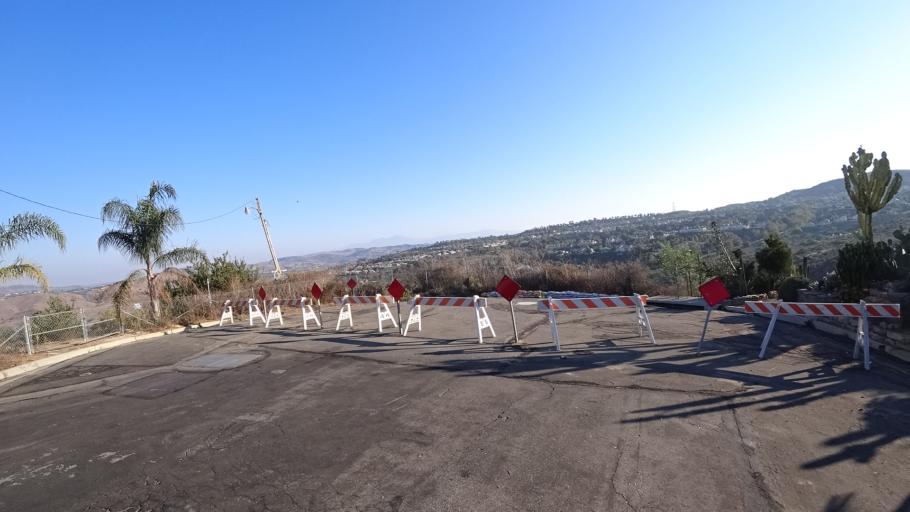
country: US
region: California
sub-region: Orange County
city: San Clemente
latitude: 33.4354
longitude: -117.6023
